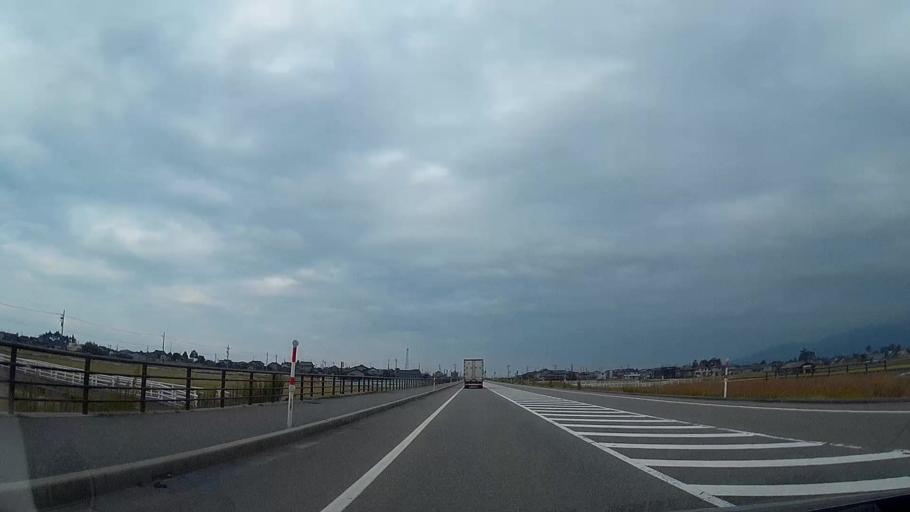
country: JP
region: Toyama
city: Nyuzen
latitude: 36.9179
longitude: 137.4636
